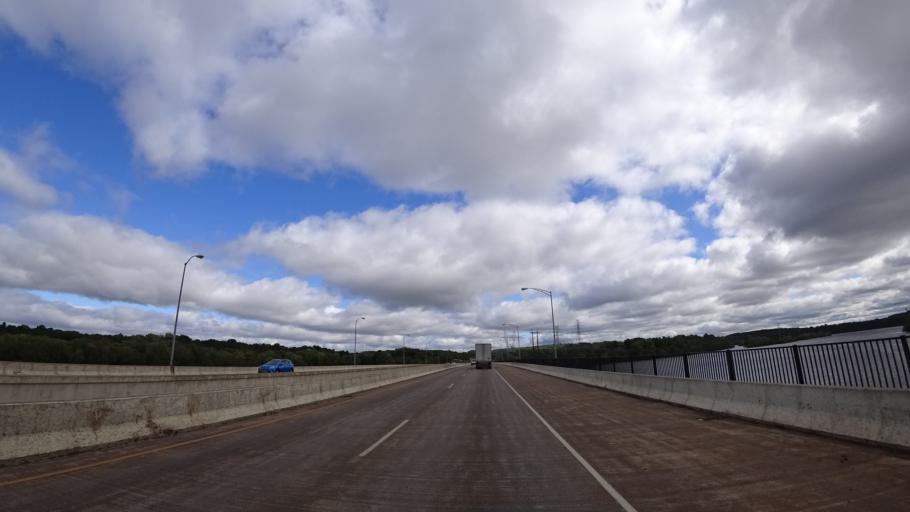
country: US
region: Wisconsin
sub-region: Eau Claire County
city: Eau Claire
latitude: 44.8410
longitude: -91.5003
